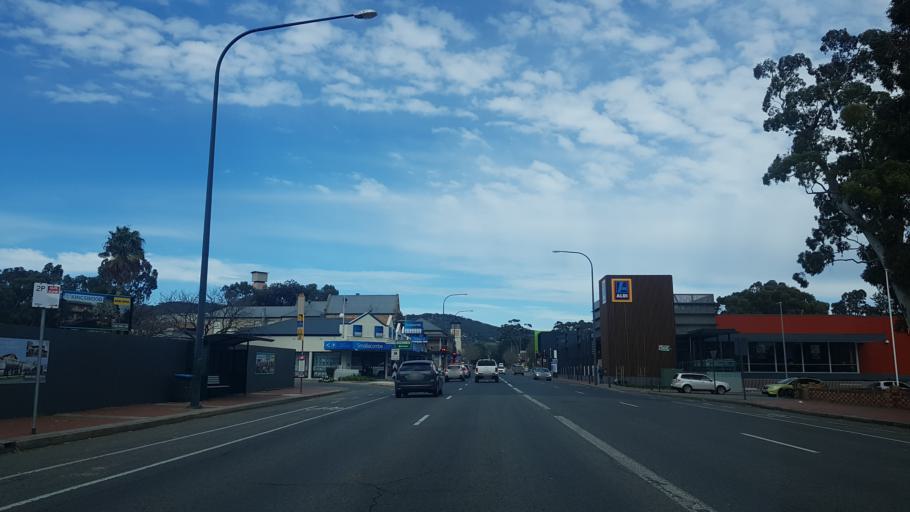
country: AU
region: South Australia
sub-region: Mitcham
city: Hawthorn
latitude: -34.9730
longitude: 138.6092
